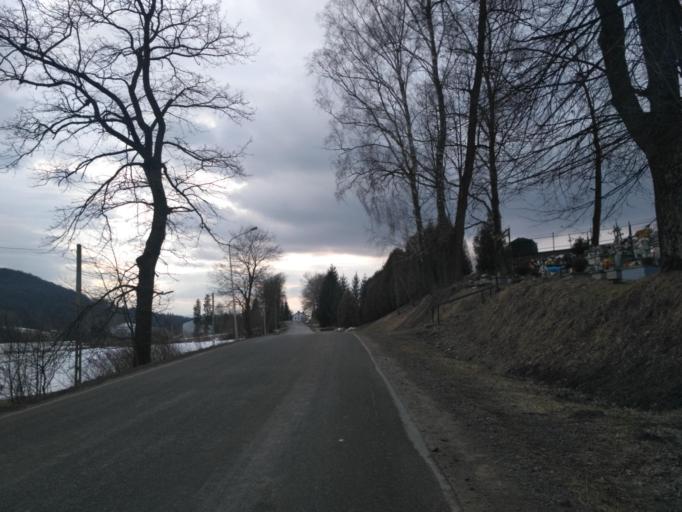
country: PL
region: Subcarpathian Voivodeship
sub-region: Powiat brzozowski
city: Dydnia
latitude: 49.6234
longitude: 22.1541
